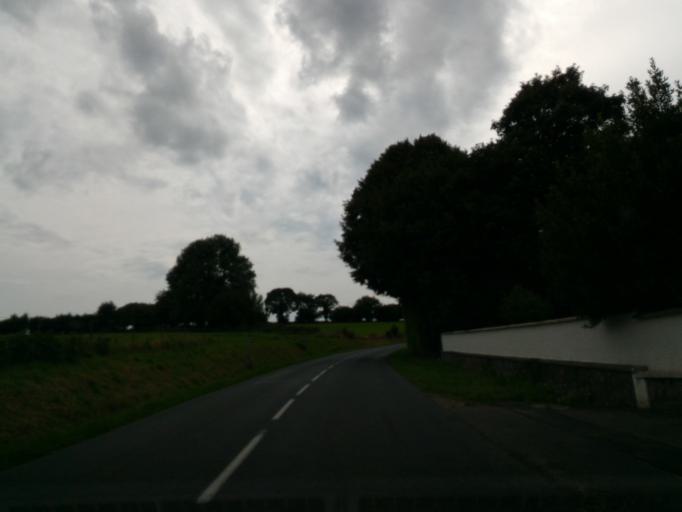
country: FR
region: Lower Normandy
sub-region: Departement de la Manche
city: La Haye-Pesnel
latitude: 48.7874
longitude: -1.4116
